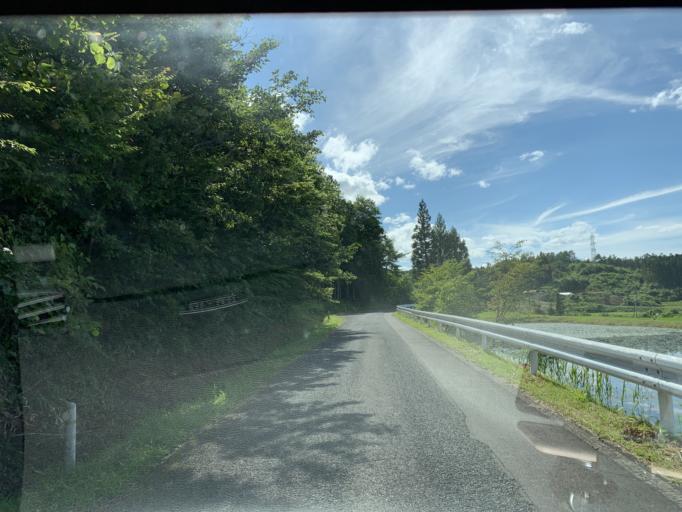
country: JP
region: Iwate
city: Ichinoseki
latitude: 38.9215
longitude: 140.9983
